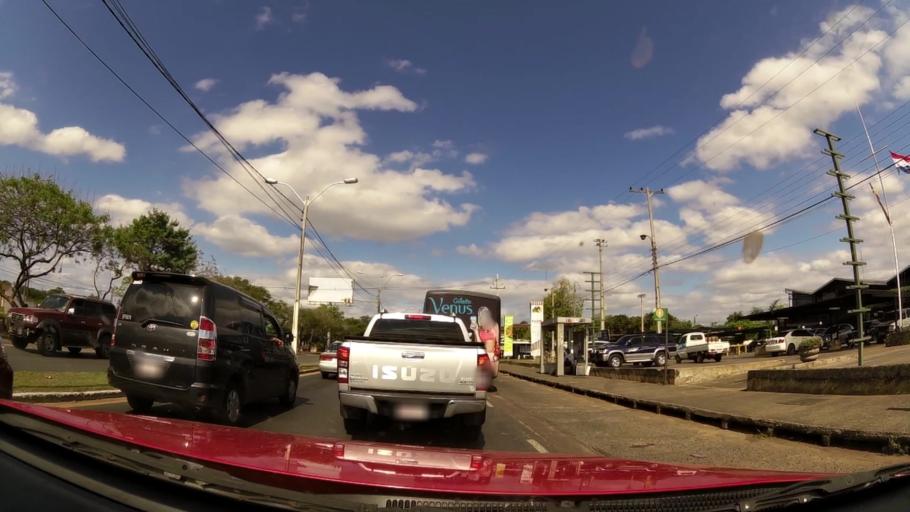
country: PY
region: Central
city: San Lorenzo
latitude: -25.2647
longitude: -57.5058
